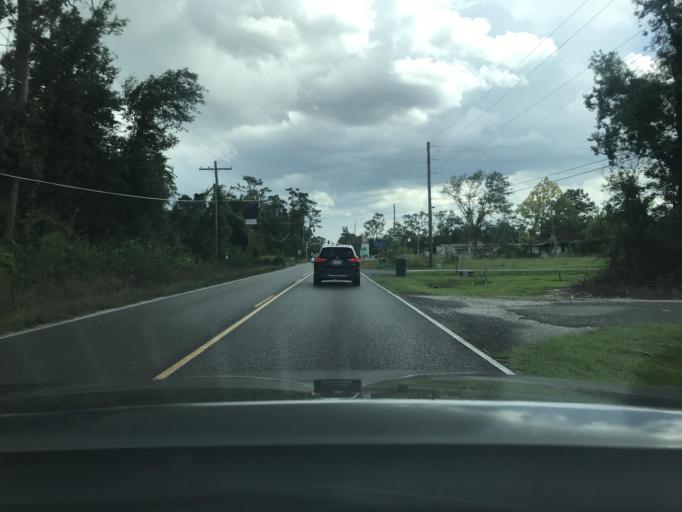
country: US
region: Louisiana
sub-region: Calcasieu Parish
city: Westlake
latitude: 30.2868
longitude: -93.2498
